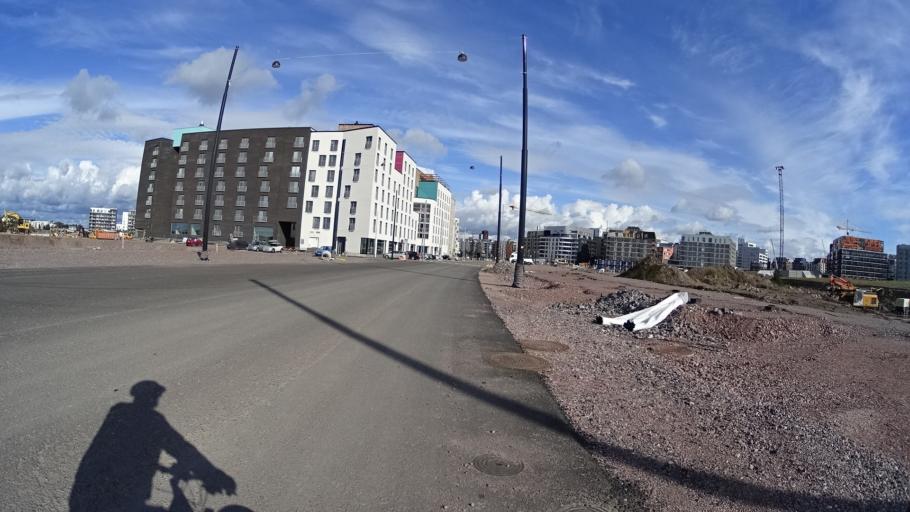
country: FI
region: Uusimaa
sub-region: Helsinki
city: Helsinki
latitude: 60.1545
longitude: 24.9099
